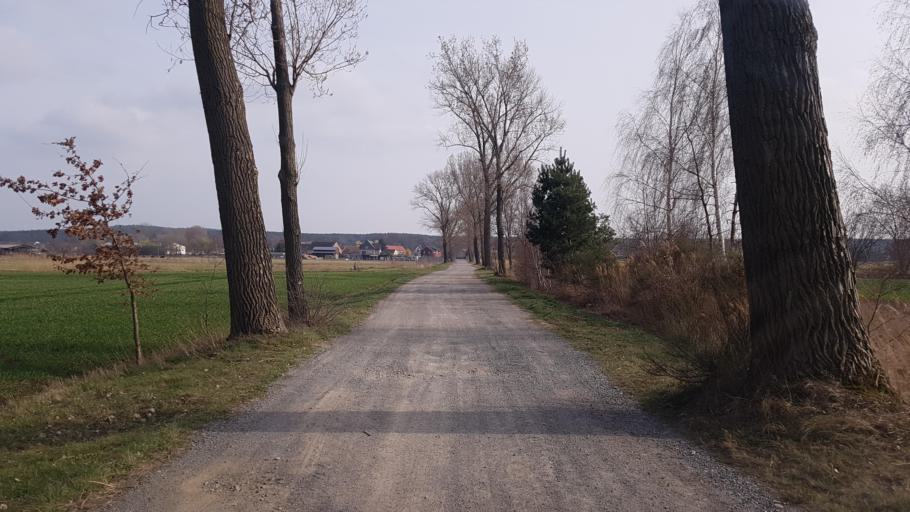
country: DE
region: Brandenburg
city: Merzdorf
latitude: 51.4102
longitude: 13.5288
